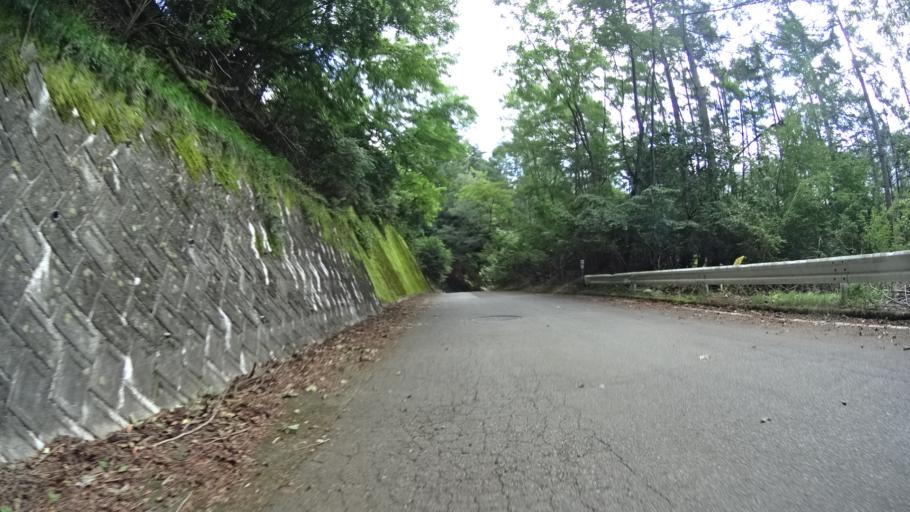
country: JP
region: Yamanashi
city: Enzan
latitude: 35.6185
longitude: 138.7753
